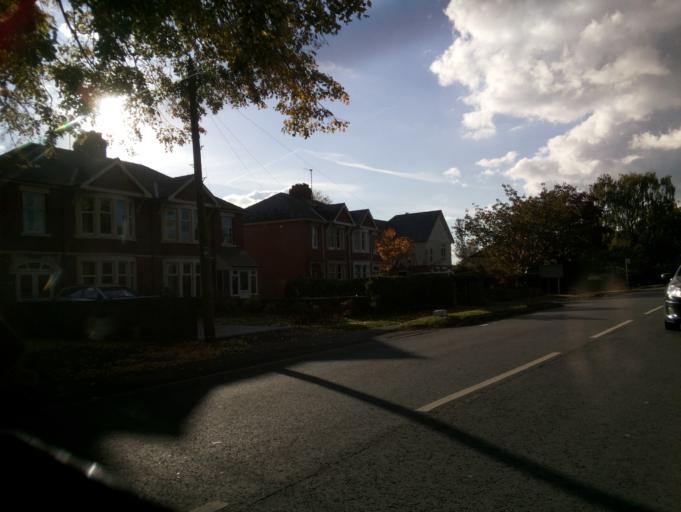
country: GB
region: England
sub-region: Herefordshire
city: Credenhill
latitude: 52.0691
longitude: -2.7721
